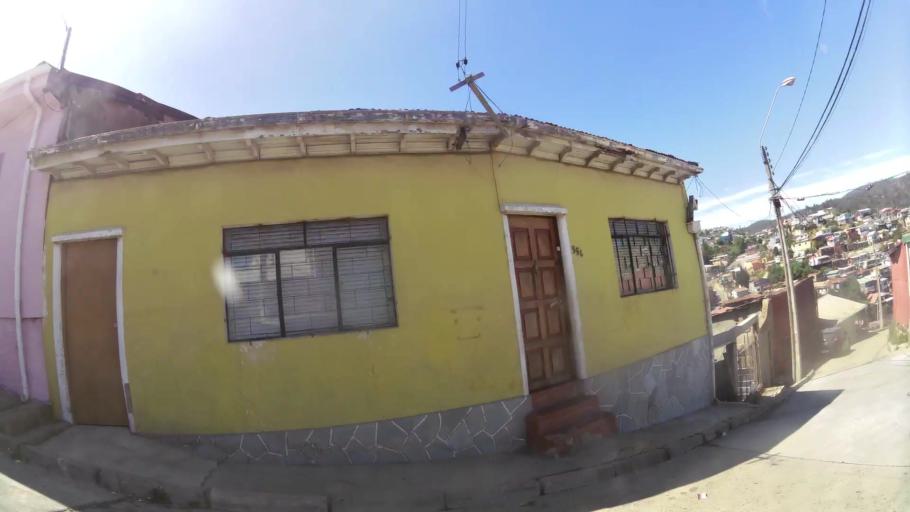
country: CL
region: Valparaiso
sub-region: Provincia de Valparaiso
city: Valparaiso
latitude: -33.0516
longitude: -71.5974
